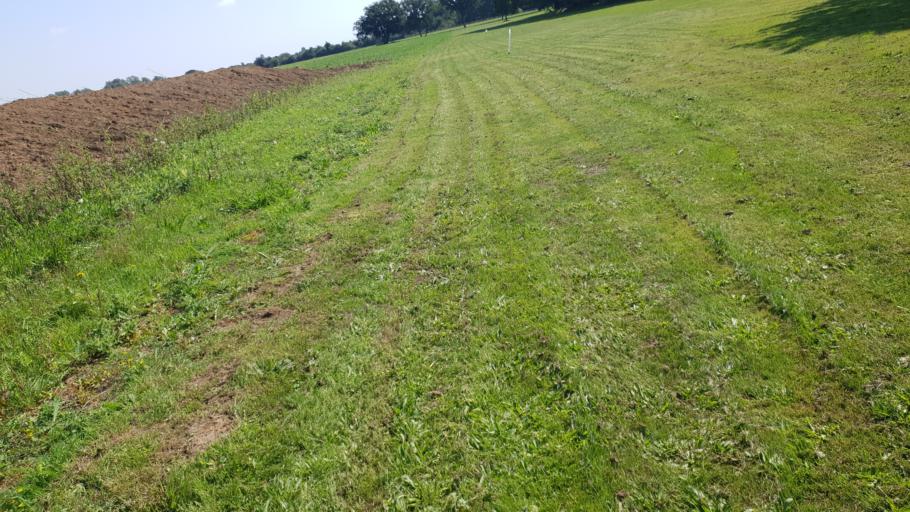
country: GB
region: England
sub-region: Essex
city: Colchester
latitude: 51.9229
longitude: 0.9507
